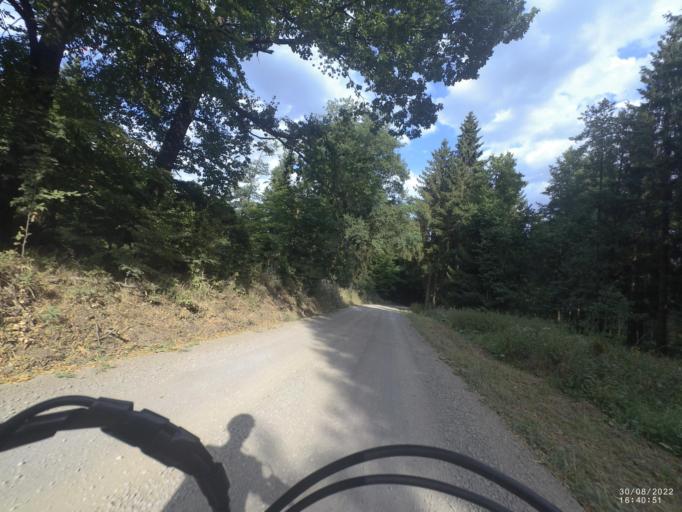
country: DE
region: Rheinland-Pfalz
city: Reuth
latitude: 50.3122
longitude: 6.4907
